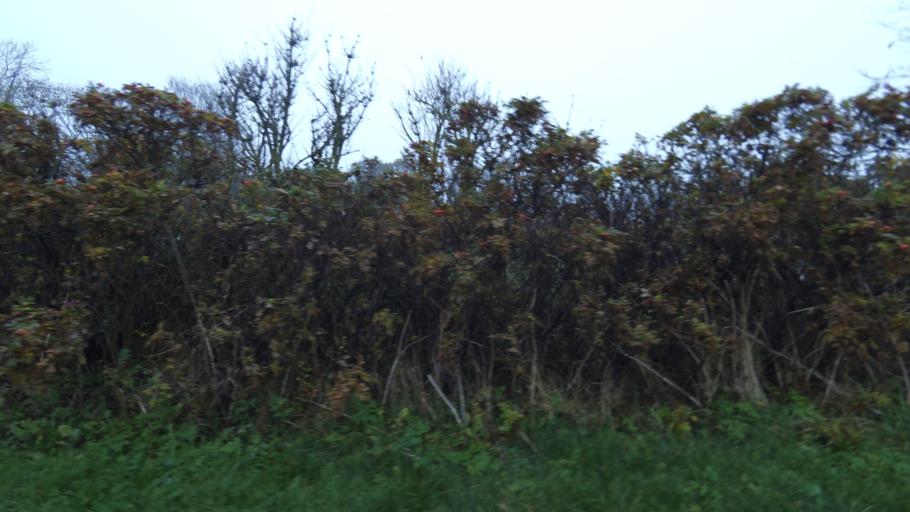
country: DK
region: Central Jutland
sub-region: Odder Kommune
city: Odder
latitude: 55.9325
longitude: 10.2578
